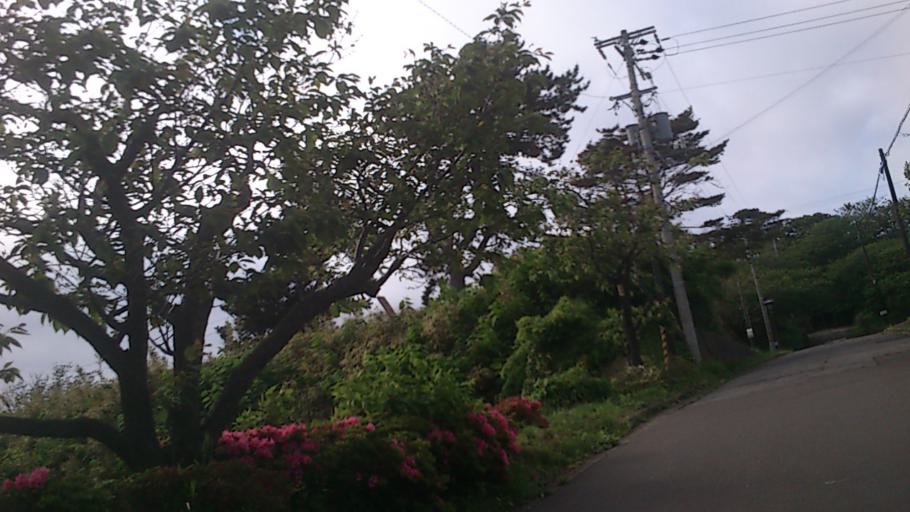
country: JP
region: Hokkaido
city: Kamiiso
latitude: 41.4283
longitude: 140.1083
